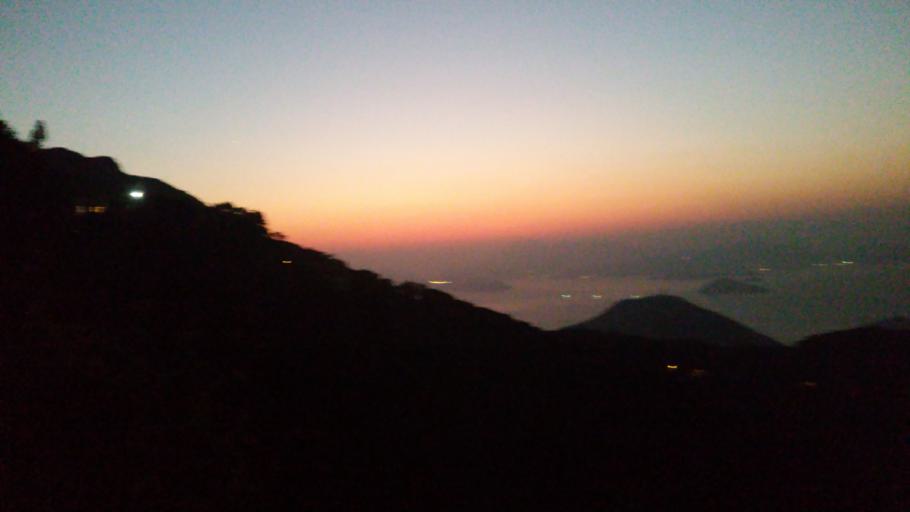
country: HK
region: Central and Western
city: Central
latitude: 22.2760
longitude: 114.1419
